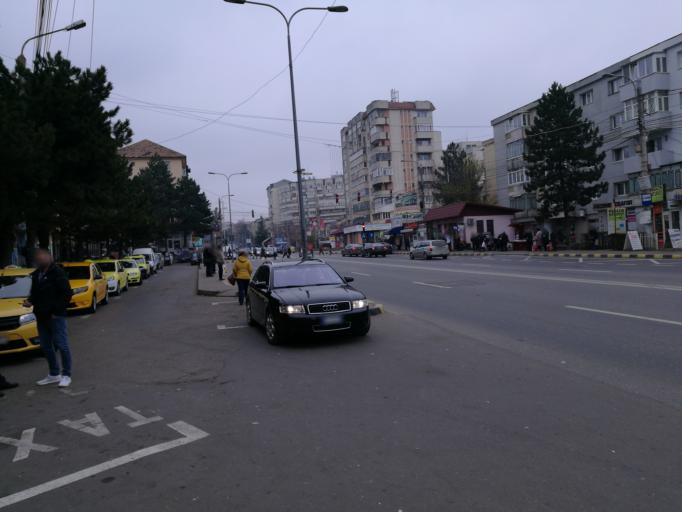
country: RO
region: Suceava
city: Suceava
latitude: 47.6713
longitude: 26.2779
